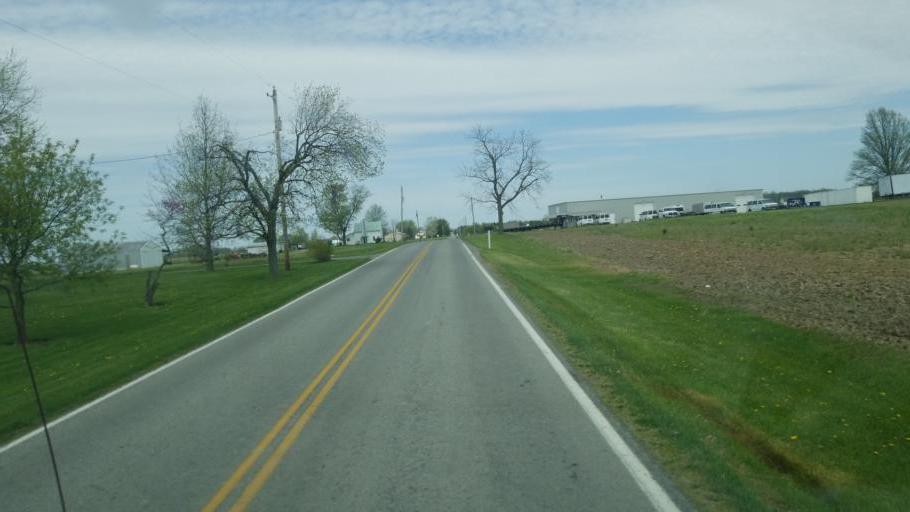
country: US
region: Ohio
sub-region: Allen County
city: Bluffton
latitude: 40.8035
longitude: -83.9758
